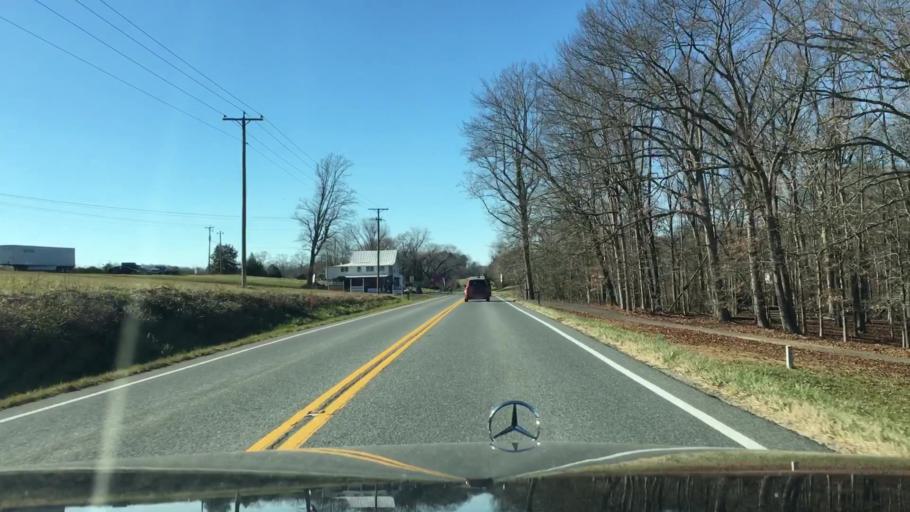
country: US
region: Virginia
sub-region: Franklin County
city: North Shore
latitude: 37.2424
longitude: -79.6724
